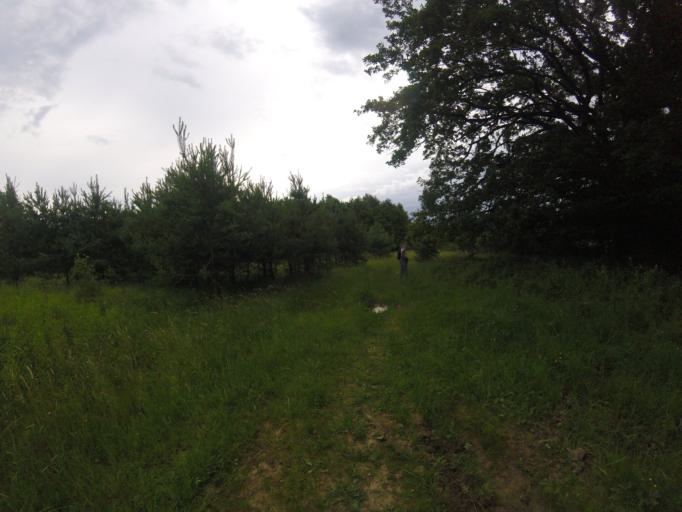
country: SI
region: Hodos-Hodos
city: Hodos
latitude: 46.8420
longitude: 16.4410
